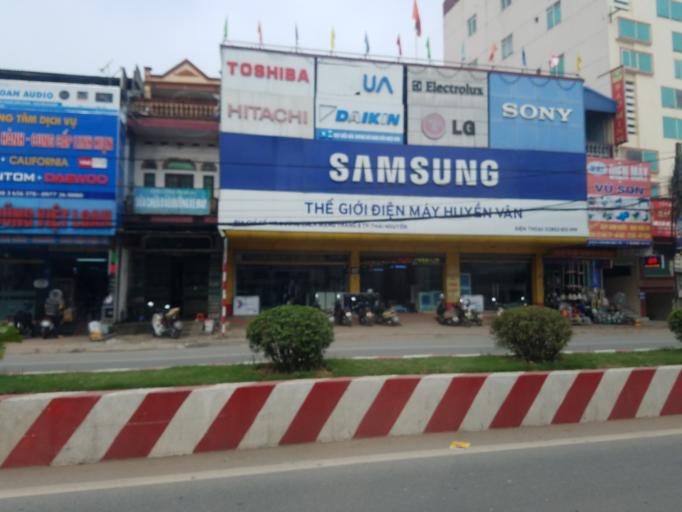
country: VN
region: Thai Nguyen
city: Thanh Pho Thai Nguyen
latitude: 21.5910
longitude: 105.8452
